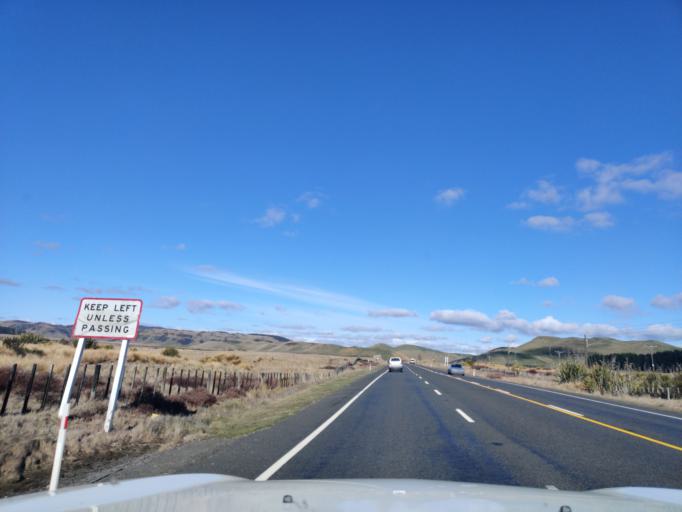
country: NZ
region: Manawatu-Wanganui
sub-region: Ruapehu District
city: Waiouru
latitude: -39.4898
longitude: 175.6707
